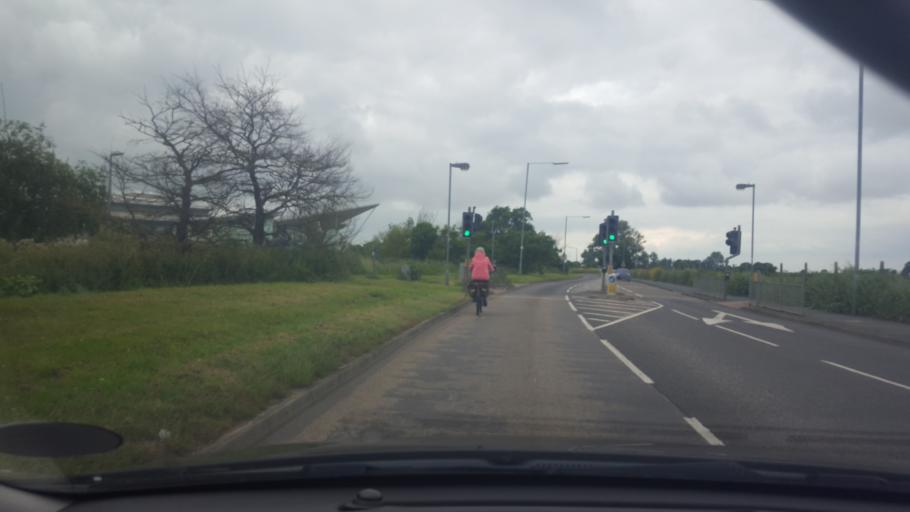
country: GB
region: England
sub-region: Essex
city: Clacton-on-Sea
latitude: 51.7933
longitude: 1.1194
